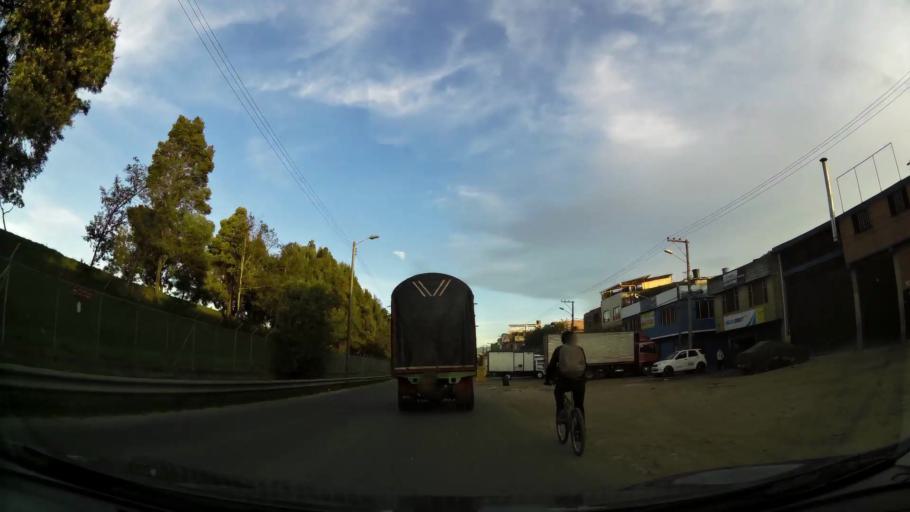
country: CO
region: Cundinamarca
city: Funza
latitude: 4.6925
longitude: -74.1482
